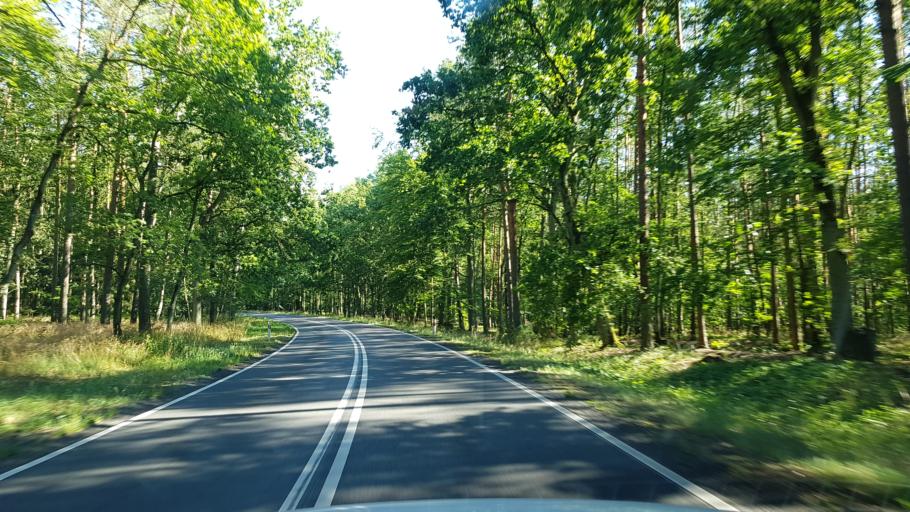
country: PL
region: West Pomeranian Voivodeship
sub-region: Powiat goleniowski
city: Stepnica
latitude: 53.6363
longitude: 14.6609
